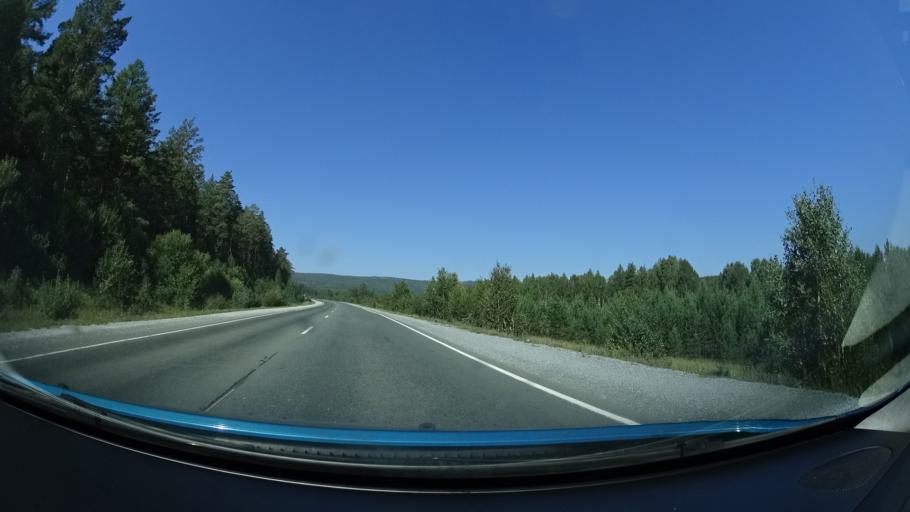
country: RU
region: Bashkortostan
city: Abzakovo
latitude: 53.8556
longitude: 58.5743
